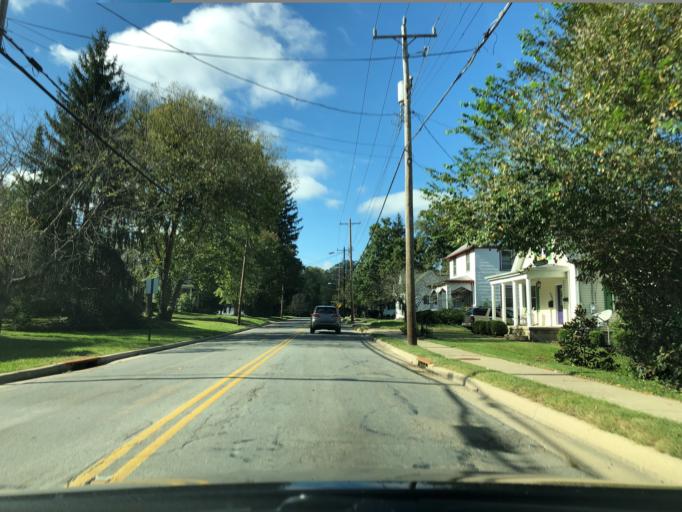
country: US
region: Ohio
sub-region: Hamilton County
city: Loveland
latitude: 39.2610
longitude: -84.2513
